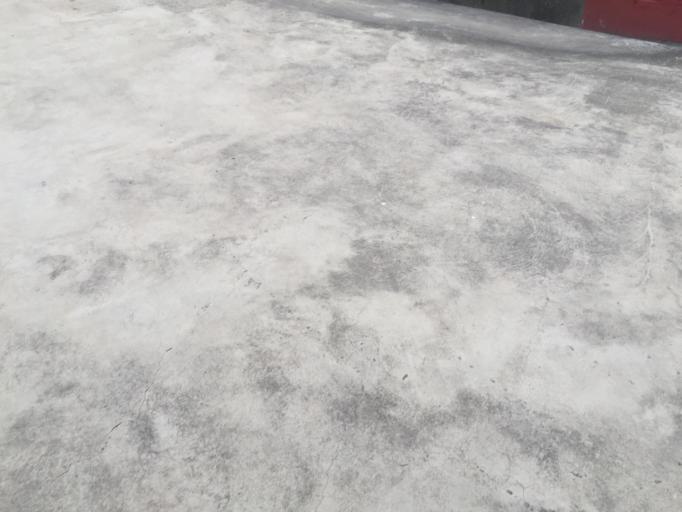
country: TW
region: Taiwan
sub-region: Miaoli
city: Miaoli
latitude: 24.5833
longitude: 120.8321
